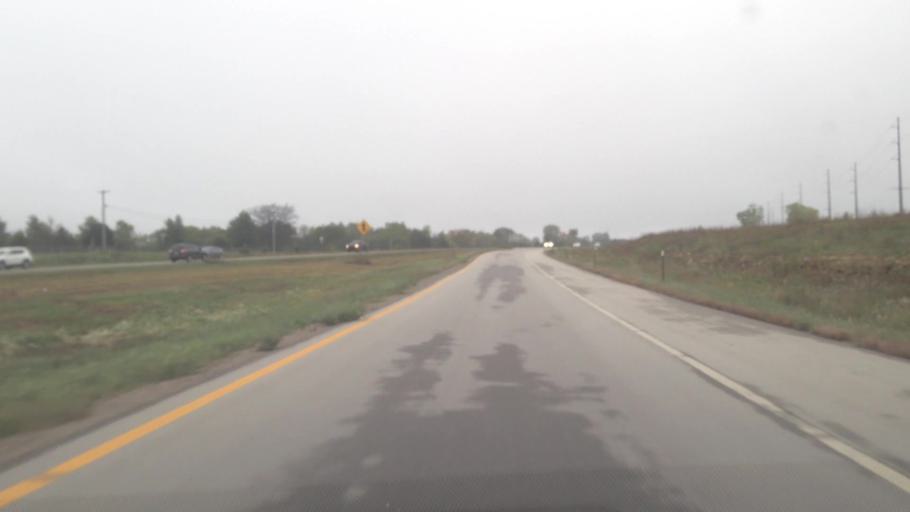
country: US
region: Kansas
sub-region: Douglas County
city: Lawrence
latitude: 38.9571
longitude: -95.3353
